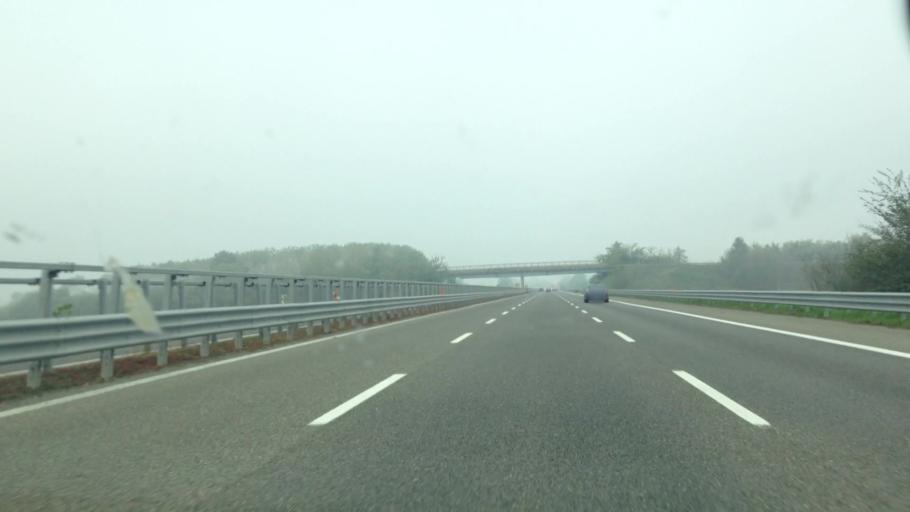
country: IT
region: Piedmont
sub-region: Provincia di Alessandria
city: Castelletto Monferrato
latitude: 44.9559
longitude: 8.5594
